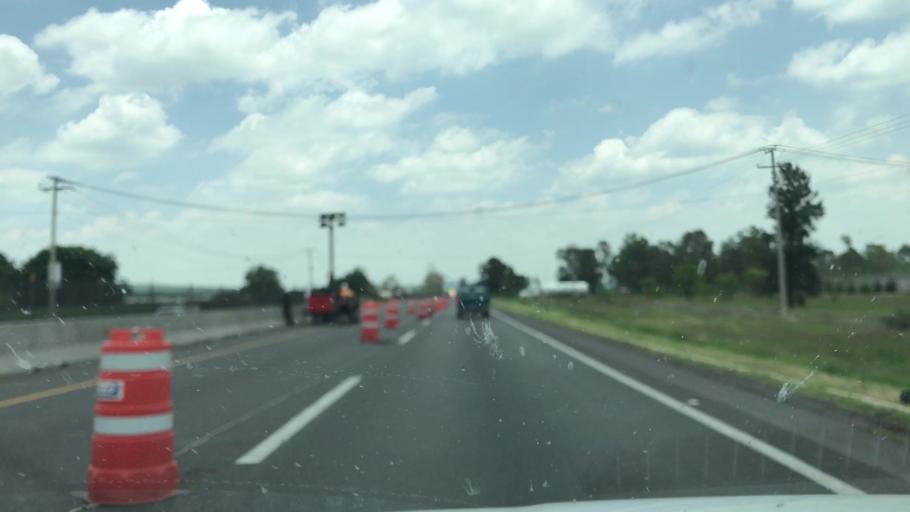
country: MX
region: Guanajuato
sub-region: Abasolo
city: San Bernardo Pena Blanca
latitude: 20.4992
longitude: -101.4804
